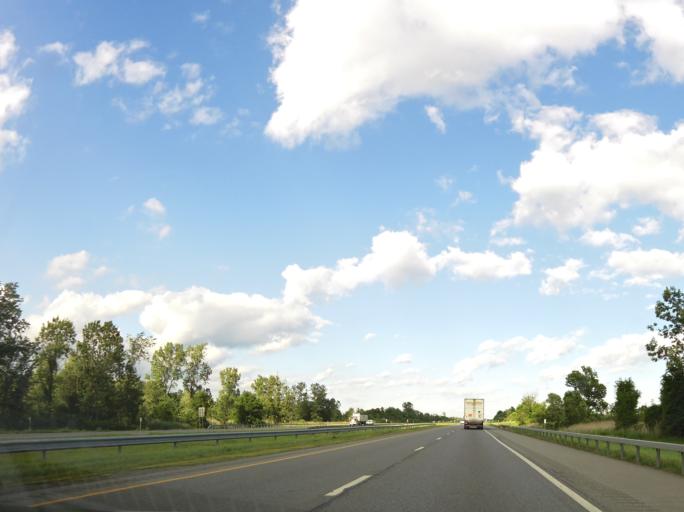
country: US
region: New York
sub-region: Genesee County
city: Oakfield
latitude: 43.0155
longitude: -78.2859
